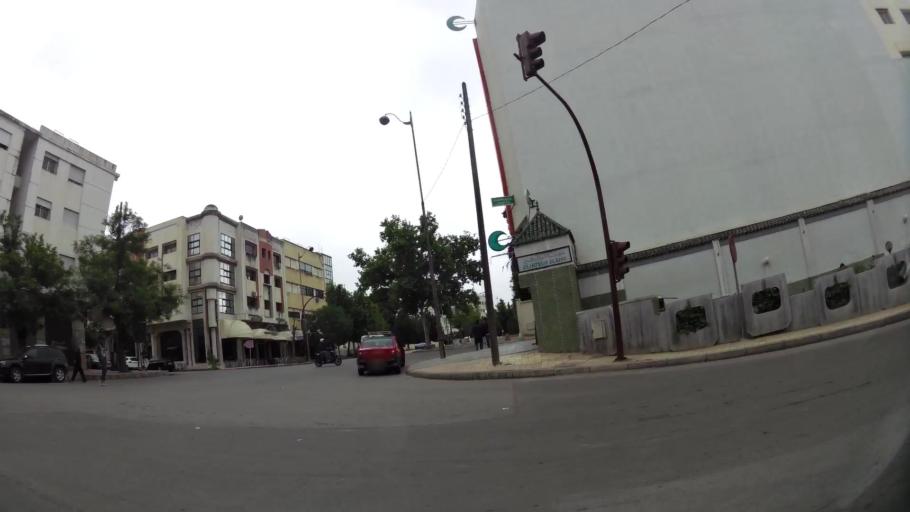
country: MA
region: Fes-Boulemane
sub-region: Fes
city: Fes
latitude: 34.0392
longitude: -4.9935
